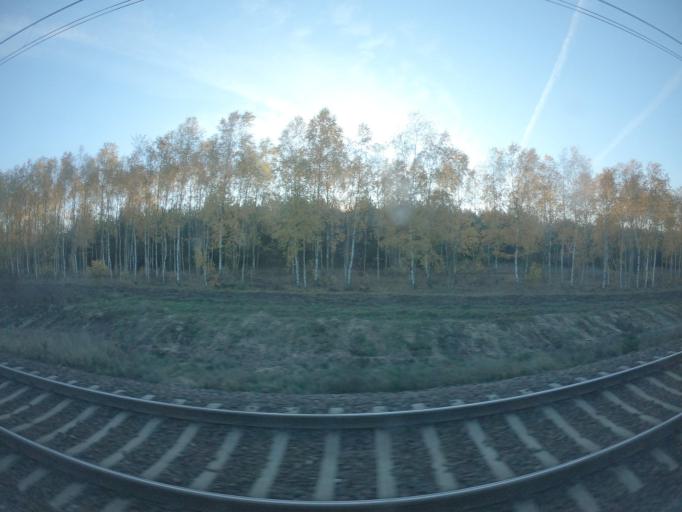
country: PL
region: Lubusz
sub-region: Powiat slubicki
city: Rzepin
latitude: 52.2868
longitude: 14.8946
